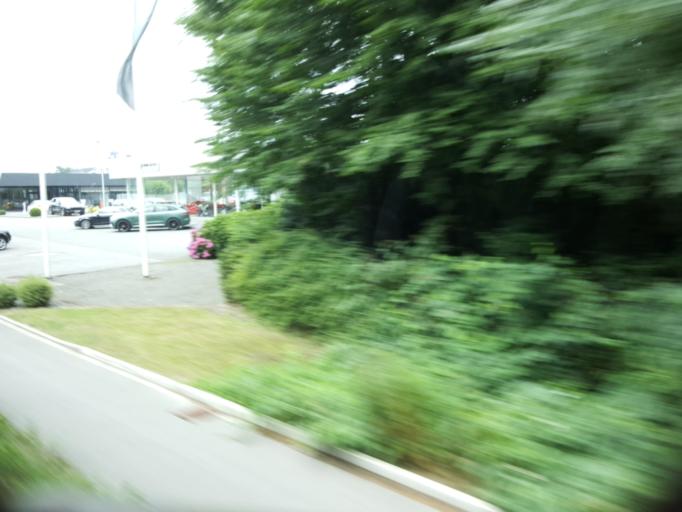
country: DE
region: North Rhine-Westphalia
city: Bad Oeynhausen
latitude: 52.2143
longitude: 8.7593
